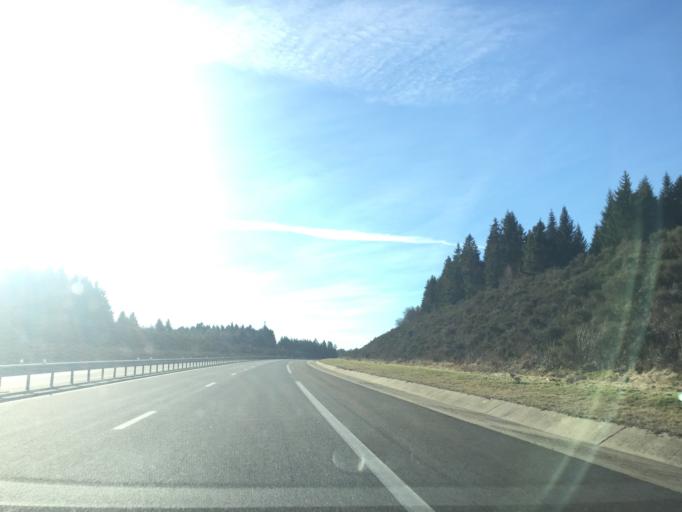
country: FR
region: Auvergne
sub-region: Departement du Puy-de-Dome
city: Gelles
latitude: 45.7587
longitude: 2.7277
